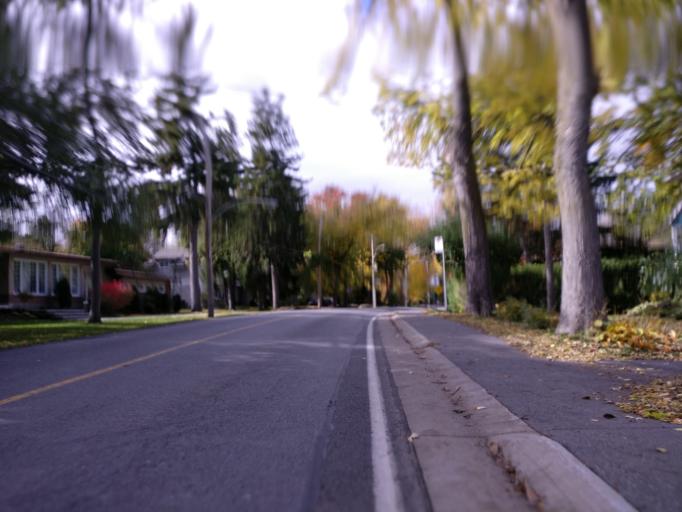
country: CA
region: Quebec
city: Baie-D'Urfe
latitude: 45.4052
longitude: -73.9276
